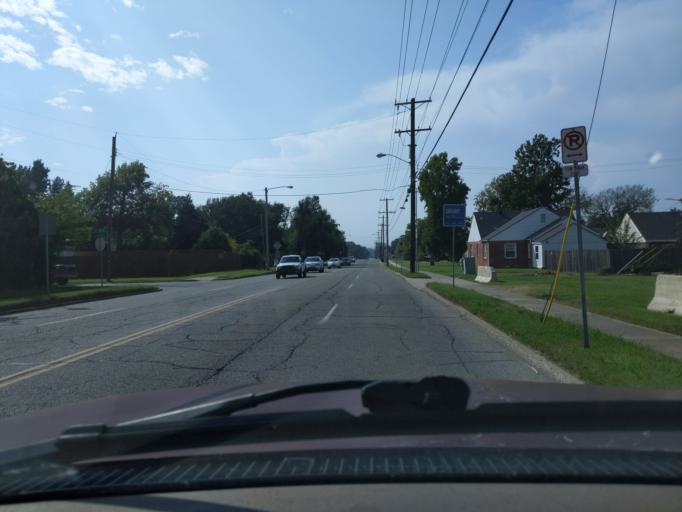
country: US
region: Oklahoma
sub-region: Tulsa County
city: Tulsa
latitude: 36.1333
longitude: -95.9360
